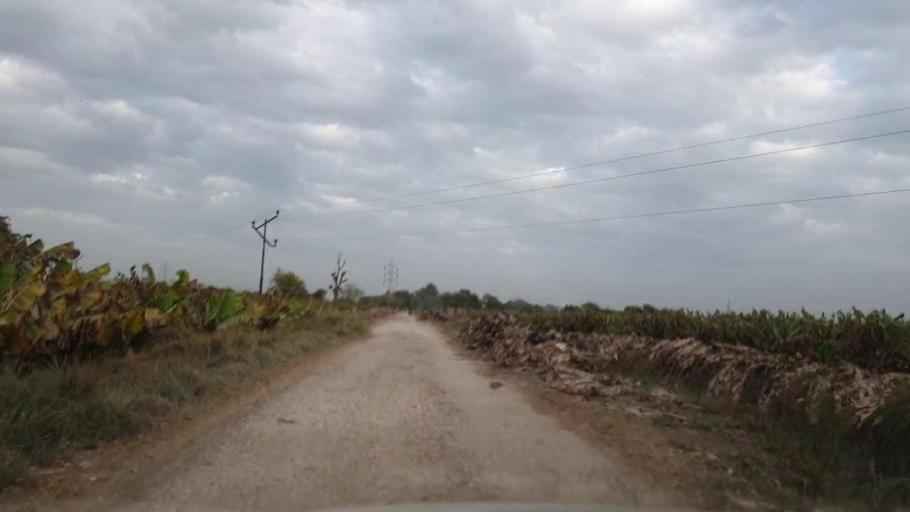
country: PK
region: Sindh
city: Matiari
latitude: 25.6240
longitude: 68.4850
